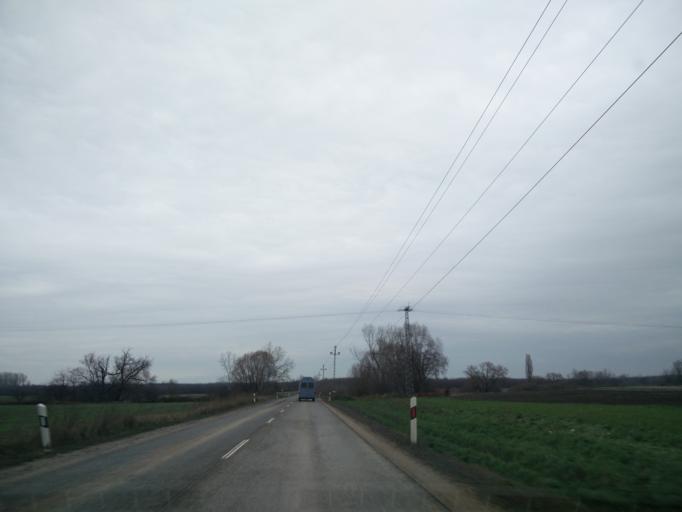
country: HU
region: Pest
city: Ullo
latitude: 47.3978
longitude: 19.3704
